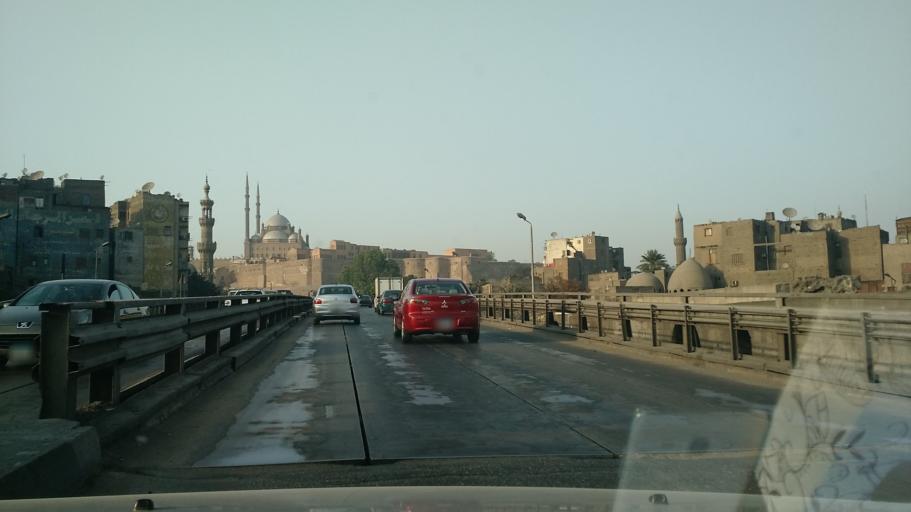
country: EG
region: Muhafazat al Qahirah
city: Cairo
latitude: 30.0230
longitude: 31.2558
